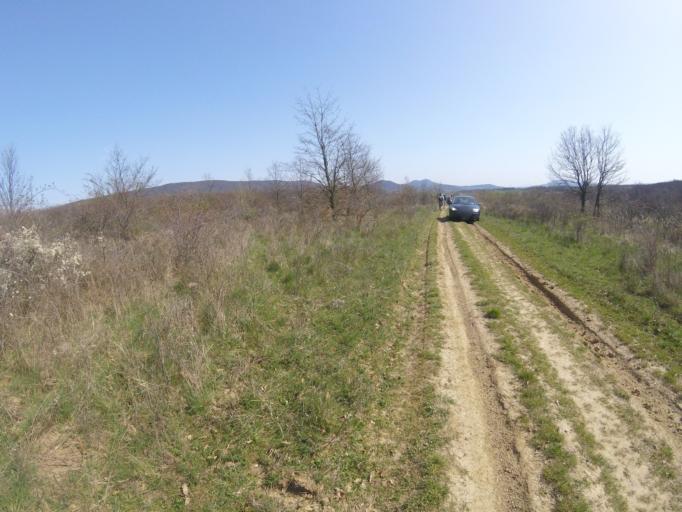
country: HU
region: Pest
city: Pilisszanto
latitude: 47.6624
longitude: 18.8696
